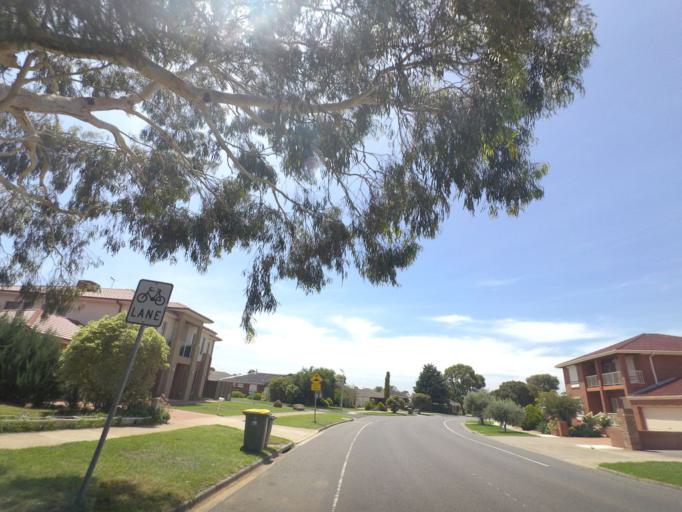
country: AU
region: Victoria
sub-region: Brimbank
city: Taylors Lakes
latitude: -37.7117
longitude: 144.7891
